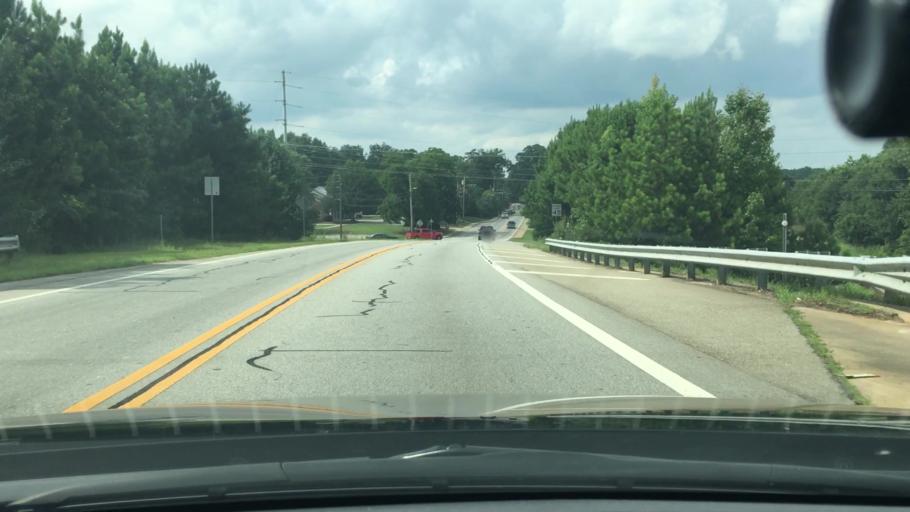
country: US
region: Georgia
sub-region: Coweta County
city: East Newnan
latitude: 33.3537
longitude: -84.7905
